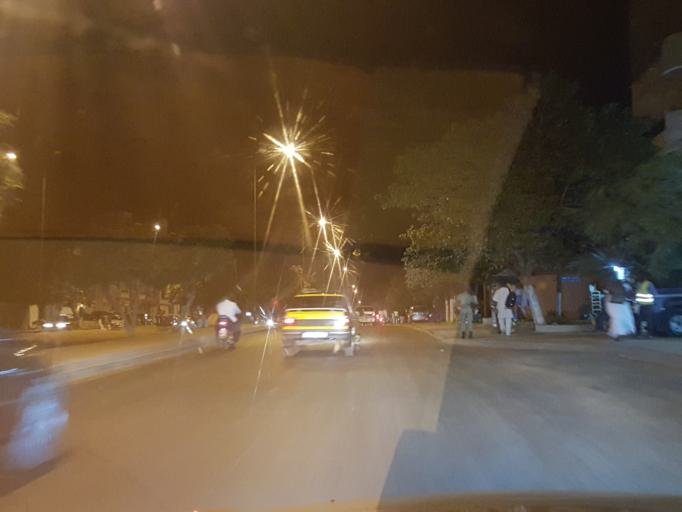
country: SN
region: Dakar
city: Grand Dakar
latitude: 14.7317
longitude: -17.4594
